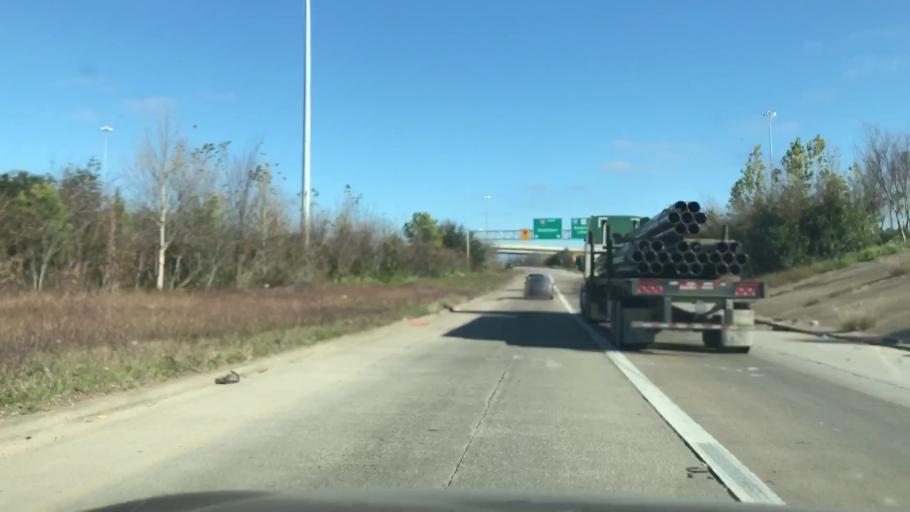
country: US
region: Texas
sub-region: Harris County
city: Jacinto City
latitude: 29.7712
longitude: -95.2646
